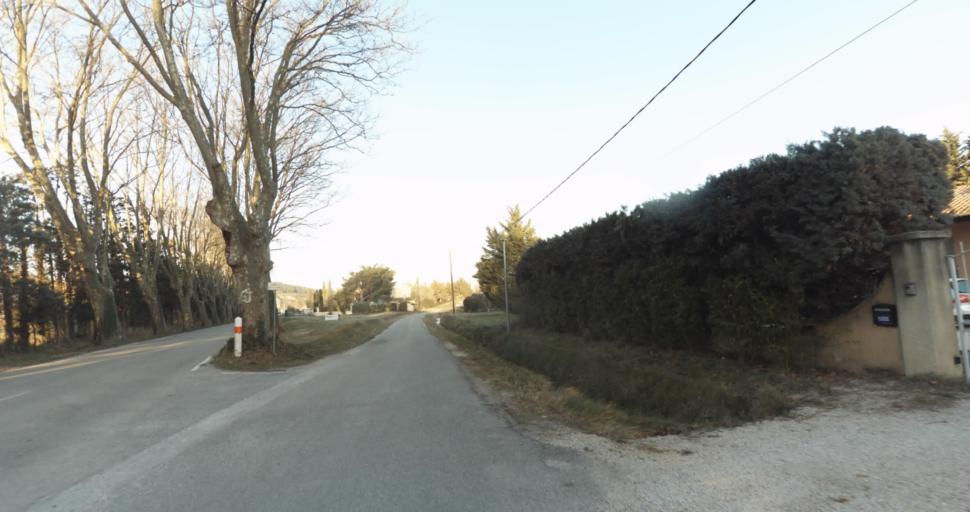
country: FR
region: Provence-Alpes-Cote d'Azur
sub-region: Departement des Bouches-du-Rhone
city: Barbentane
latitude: 43.8975
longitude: 4.7747
